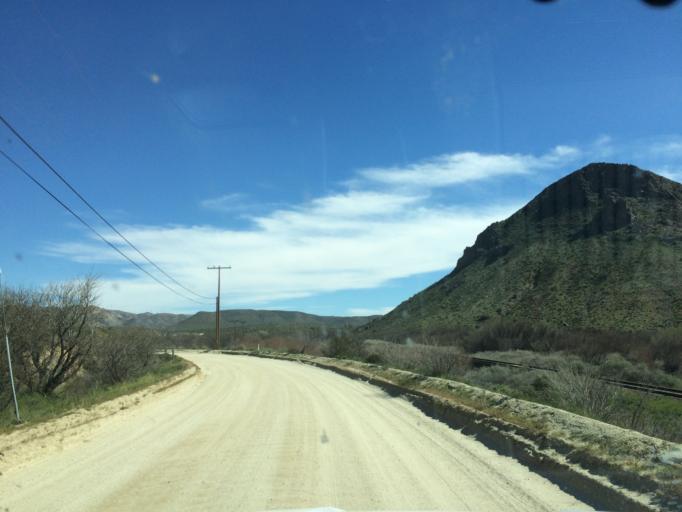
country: MX
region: Baja California
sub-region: Tecate
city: Cereso del Hongo
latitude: 32.6454
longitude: -116.1854
